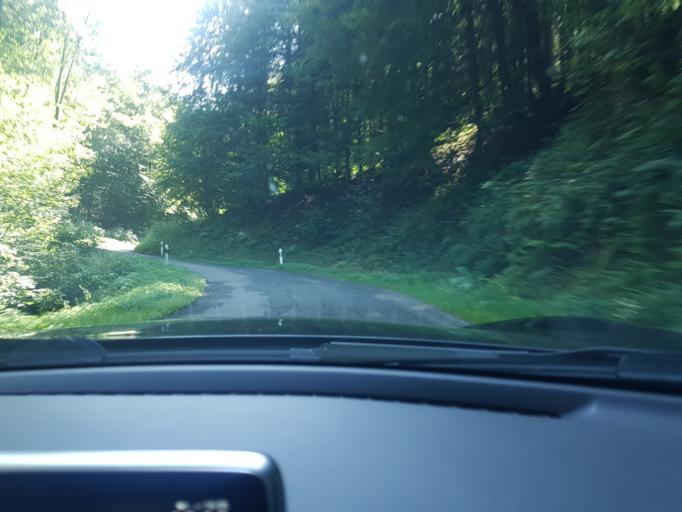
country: DE
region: Hesse
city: Hirschhorn
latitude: 49.4104
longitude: 8.8862
